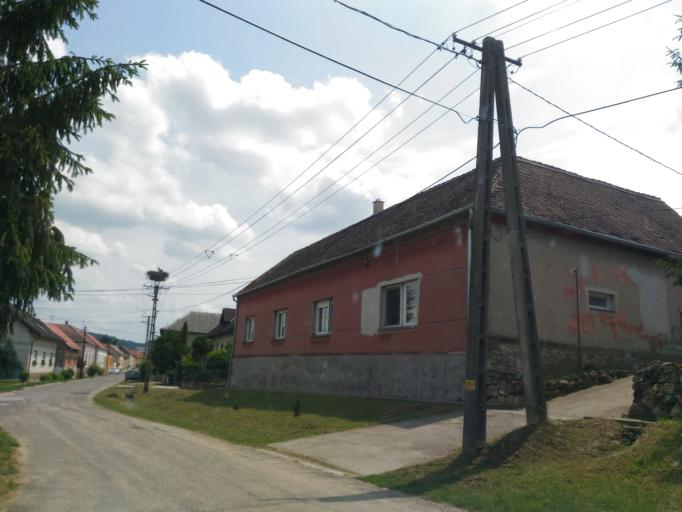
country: HU
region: Baranya
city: Komlo
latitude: 46.1971
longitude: 18.2259
